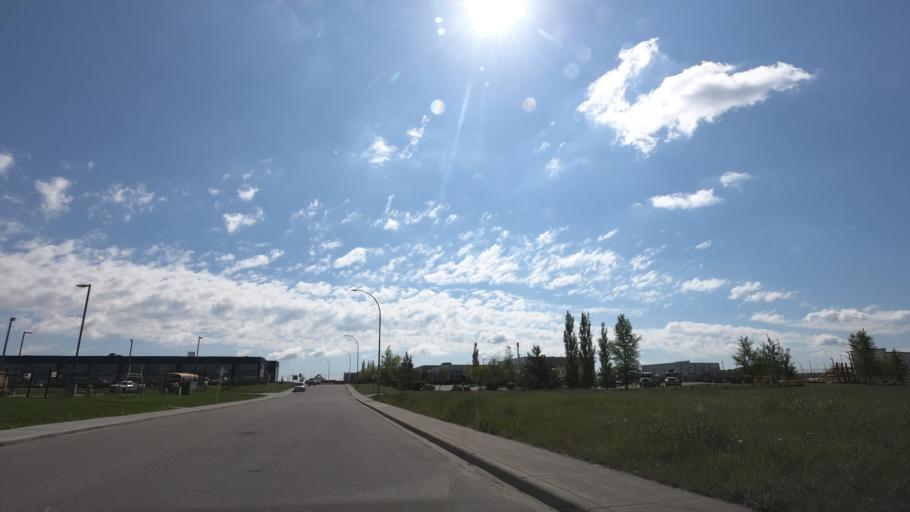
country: CA
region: Alberta
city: Airdrie
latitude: 51.3061
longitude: -114.0106
